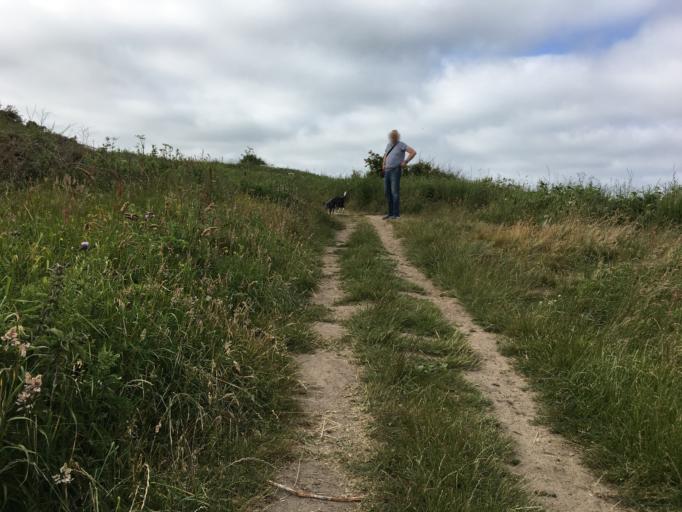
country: GB
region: England
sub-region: Northumberland
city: Alnmouth
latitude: 55.4492
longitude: -1.5881
